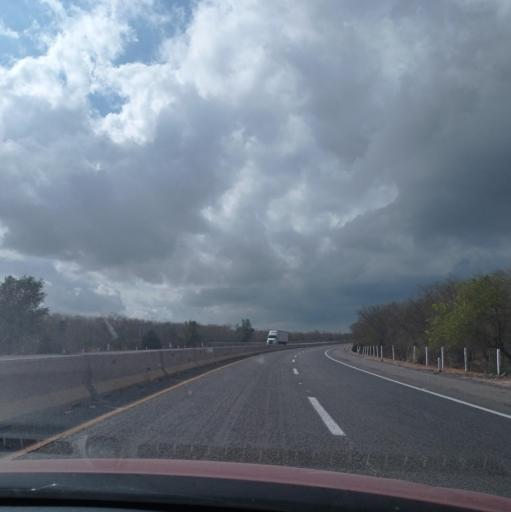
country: MX
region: Sinaloa
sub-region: Navolato
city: Juan Aldama (El Tigre)
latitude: 24.9916
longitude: -107.7731
